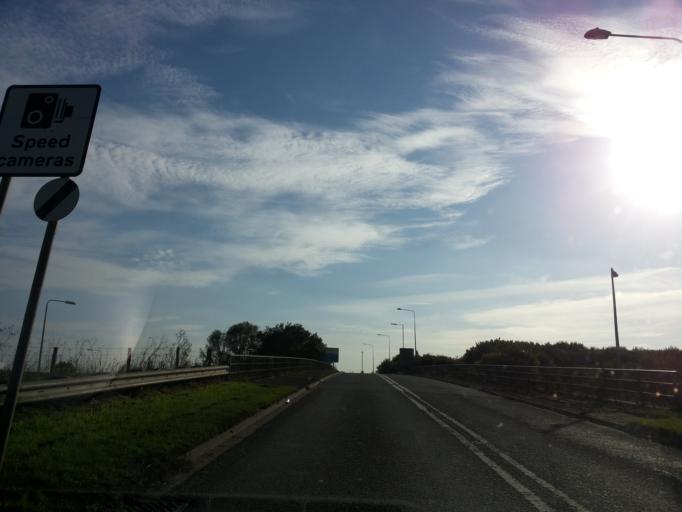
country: GB
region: England
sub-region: Doncaster
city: Hatfield
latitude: 53.5903
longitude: -0.9627
